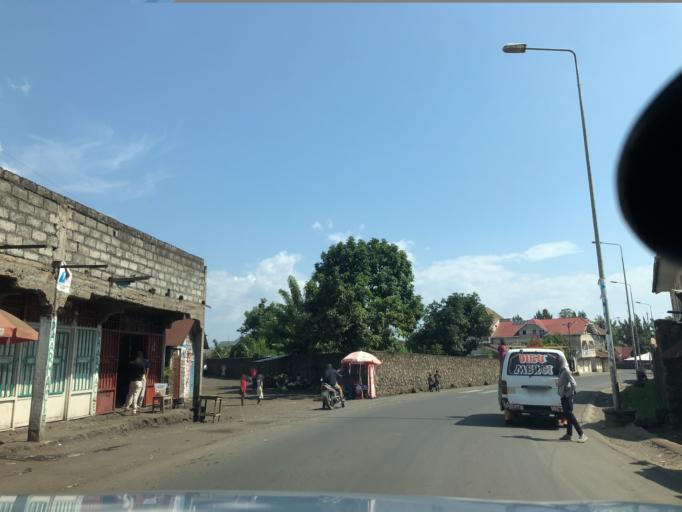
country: CD
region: Nord Kivu
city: Goma
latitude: -1.6606
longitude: 29.1731
